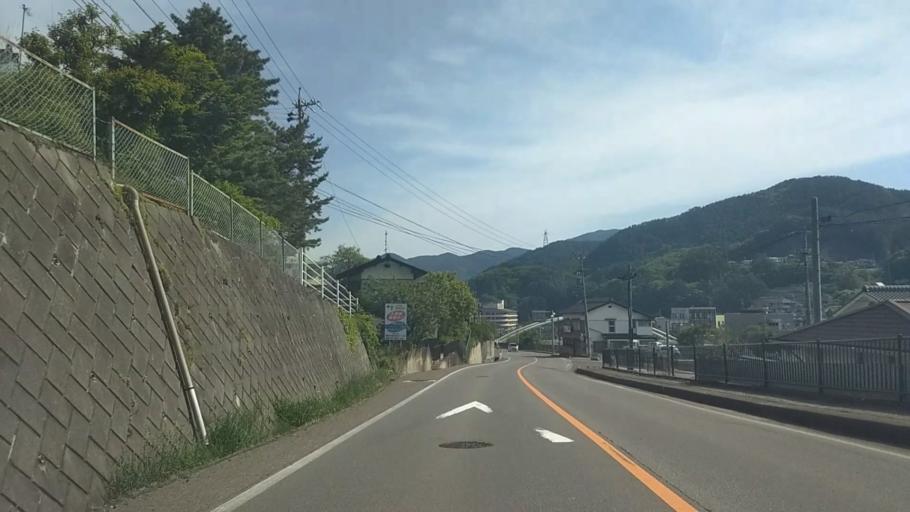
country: JP
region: Nagano
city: Saku
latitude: 36.0888
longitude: 138.4810
